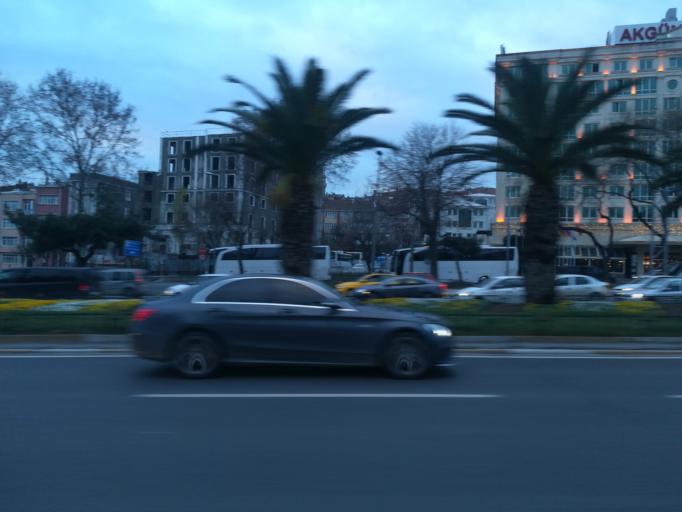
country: TR
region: Istanbul
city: Istanbul
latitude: 41.0233
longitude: 28.9314
